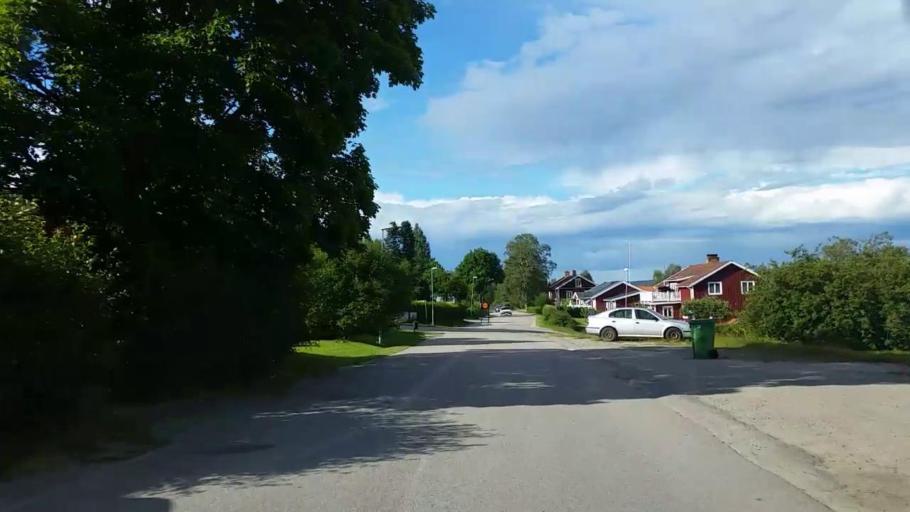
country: SE
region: Gaevleborg
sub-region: Ljusdals Kommun
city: Jaervsoe
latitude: 61.7157
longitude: 16.1669
